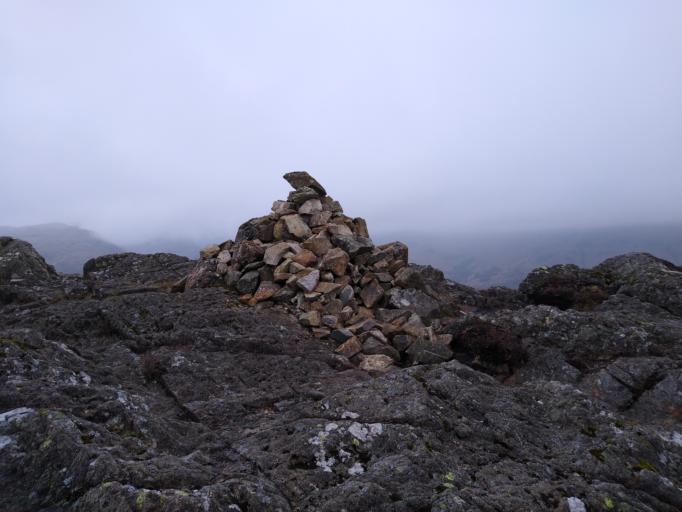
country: GB
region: England
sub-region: Cumbria
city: Keswick
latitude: 54.5222
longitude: -3.1293
